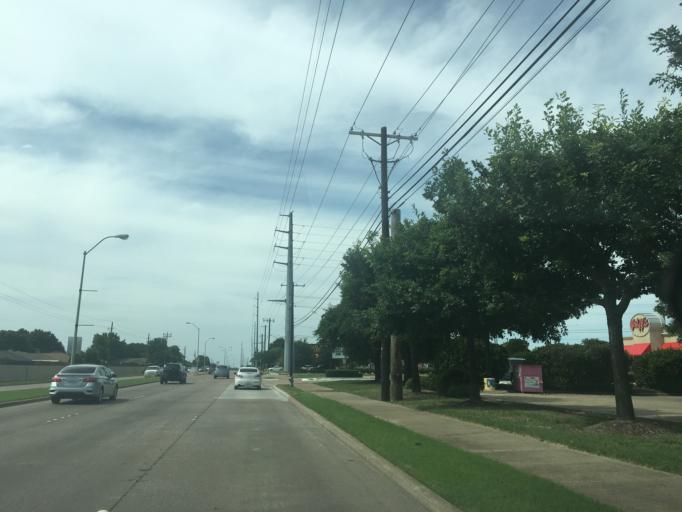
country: US
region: Texas
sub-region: Dallas County
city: Garland
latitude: 32.9327
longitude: -96.6827
